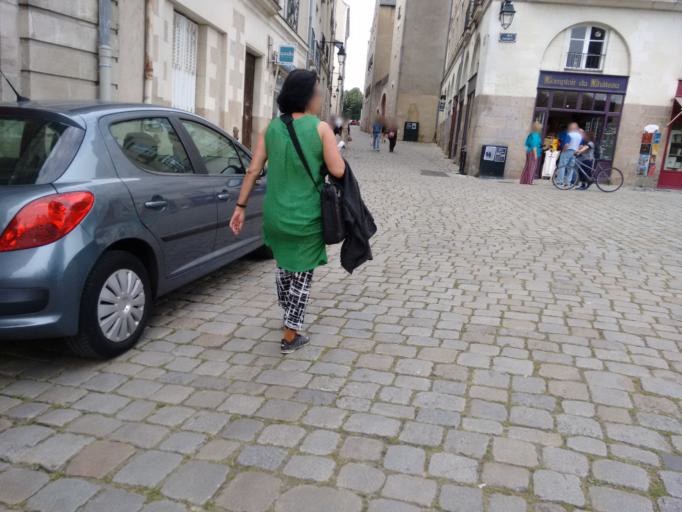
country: FR
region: Pays de la Loire
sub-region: Departement de la Loire-Atlantique
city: Nantes
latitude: 47.2166
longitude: -1.5504
